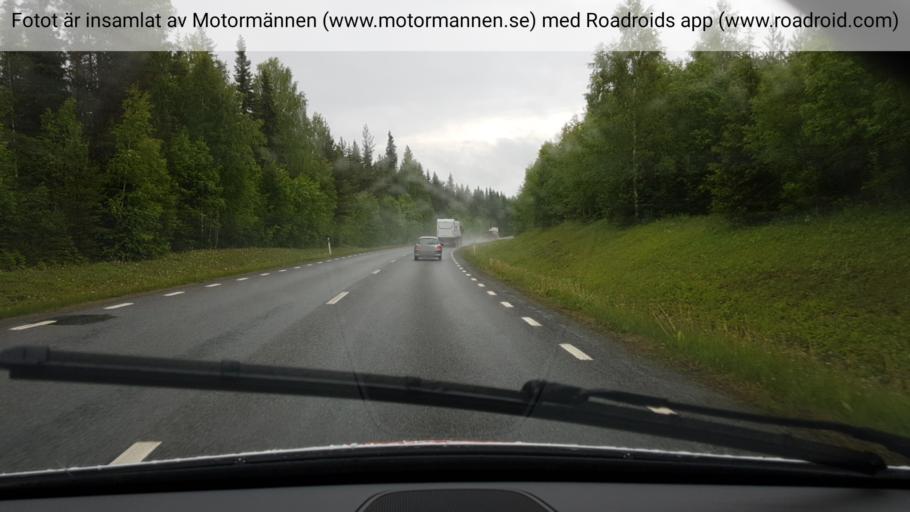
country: SE
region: Jaemtland
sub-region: Stroemsunds Kommun
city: Stroemsund
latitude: 63.5171
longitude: 15.2907
